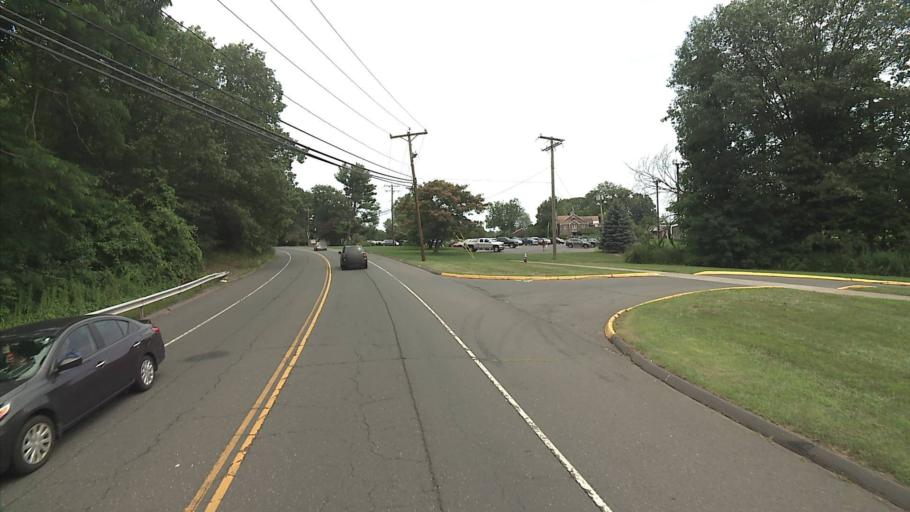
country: US
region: Connecticut
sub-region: Hartford County
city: New Britain
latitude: 41.7052
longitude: -72.7693
